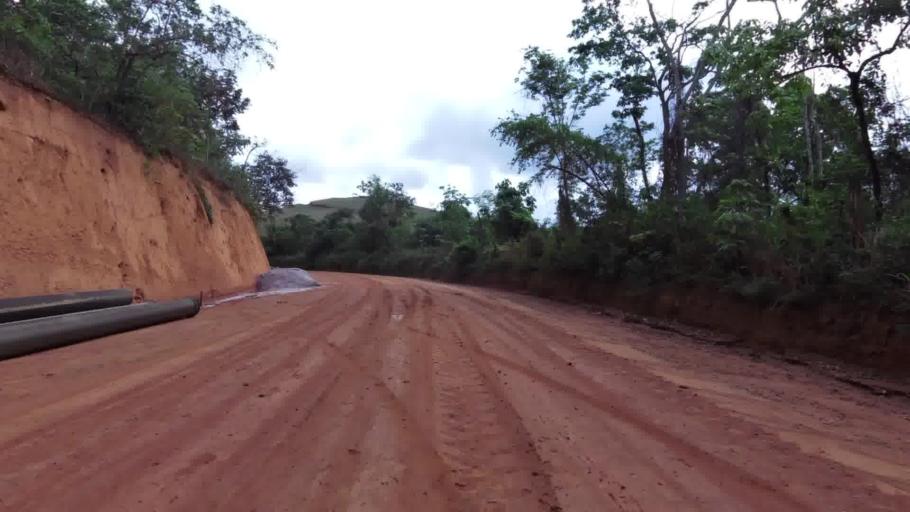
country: BR
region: Espirito Santo
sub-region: Piuma
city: Piuma
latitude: -20.8137
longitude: -40.6741
